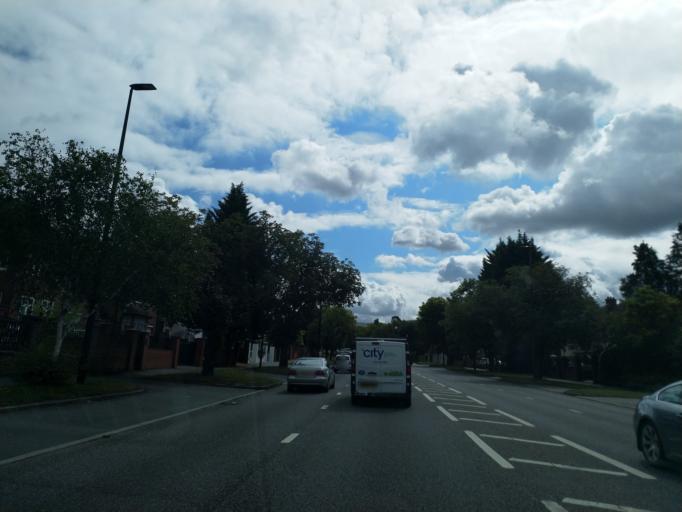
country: GB
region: England
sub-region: Greater London
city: Belsize Park
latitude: 51.5828
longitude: -0.1646
